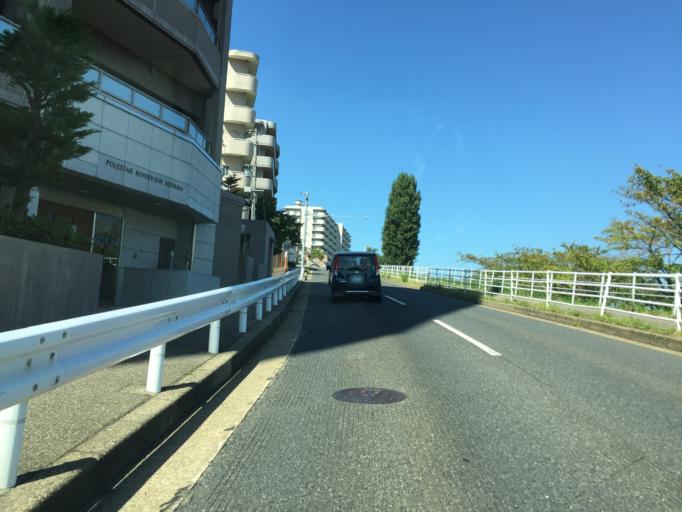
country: JP
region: Niigata
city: Niigata-shi
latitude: 37.8994
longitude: 139.0076
